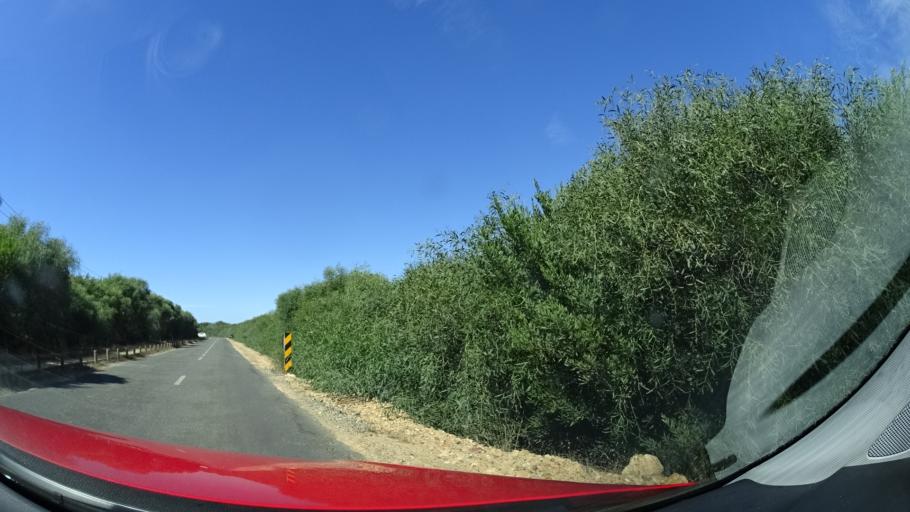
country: PT
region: Beja
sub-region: Odemira
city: Sao Teotonio
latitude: 37.5342
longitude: -8.7845
